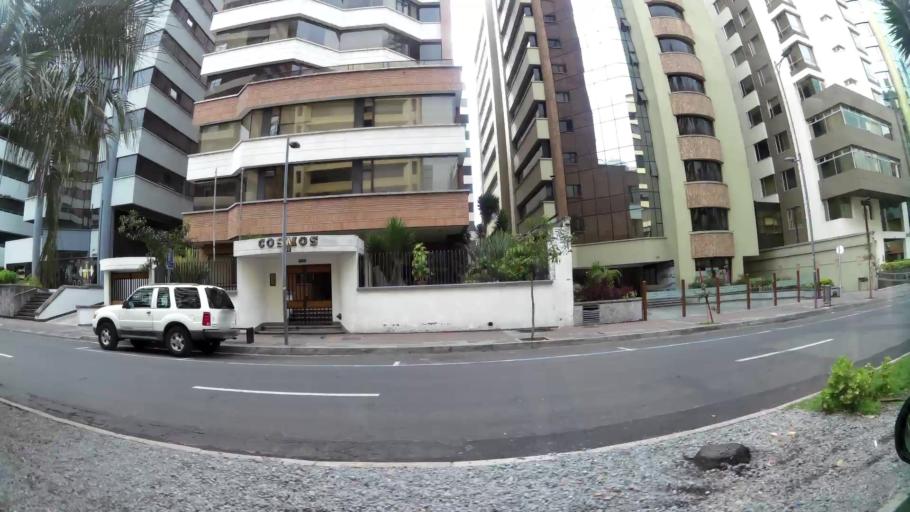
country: EC
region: Pichincha
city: Quito
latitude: -0.1802
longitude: -78.4801
